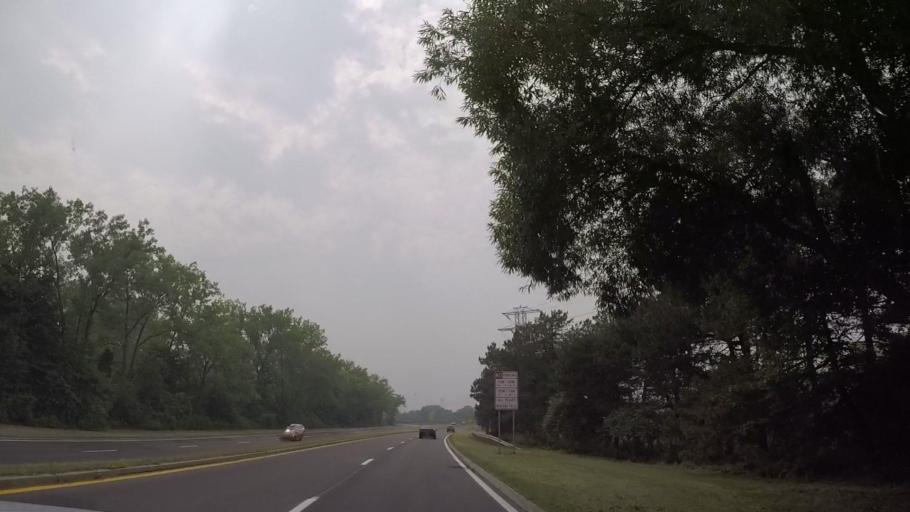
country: US
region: New York
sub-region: Niagara County
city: Niagara Falls
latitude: 43.0785
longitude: -79.0410
